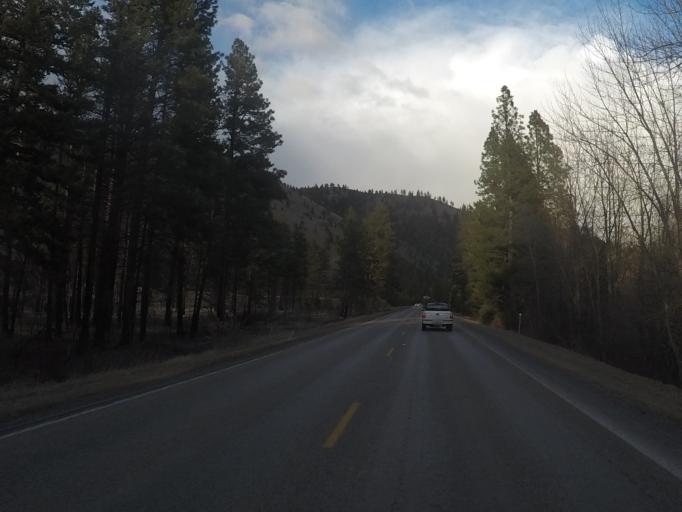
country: US
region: Montana
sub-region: Missoula County
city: Lolo
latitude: 46.7451
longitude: -114.1795
